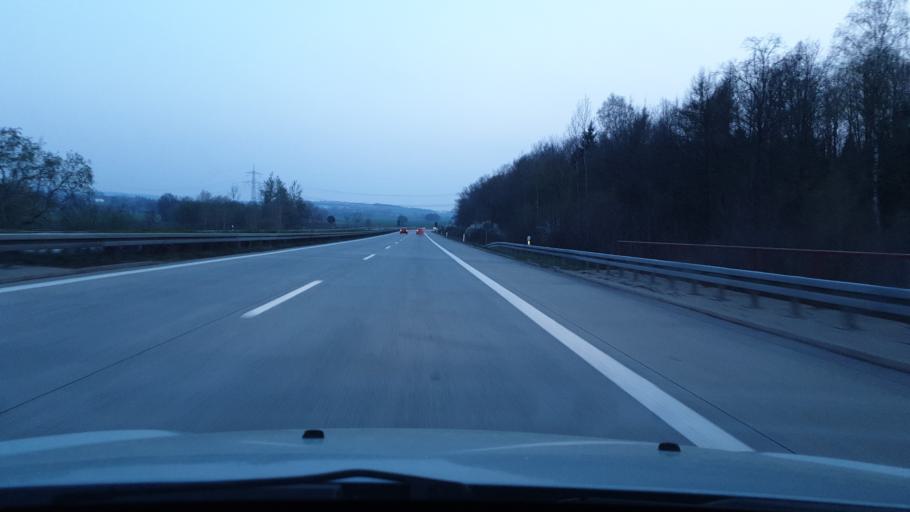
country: DE
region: Saxony
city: Niederdorf
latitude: 50.7518
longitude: 12.7996
